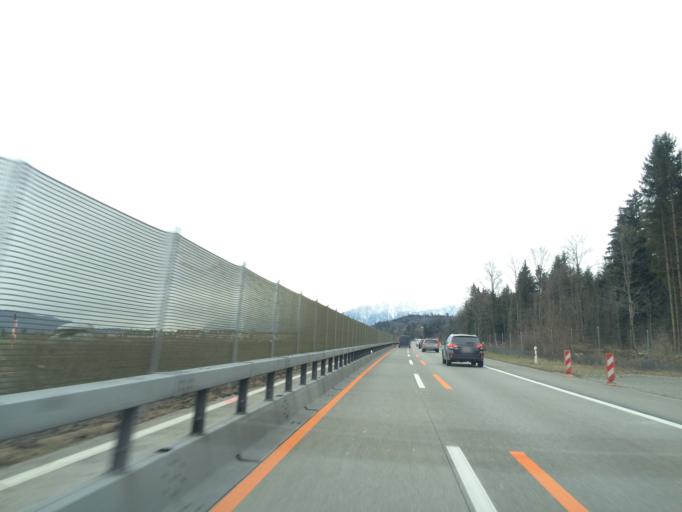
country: CH
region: Bern
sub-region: Bern-Mittelland District
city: Niederwichtrach
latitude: 46.8466
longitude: 7.5593
